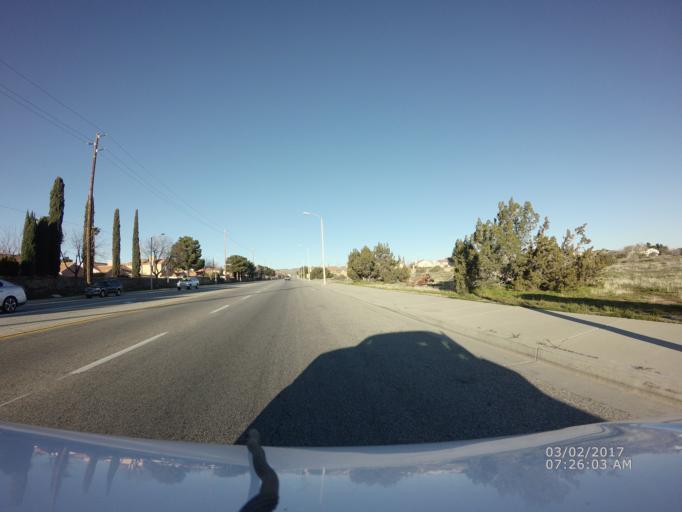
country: US
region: California
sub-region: Los Angeles County
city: Desert View Highlands
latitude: 34.6018
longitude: -118.1573
